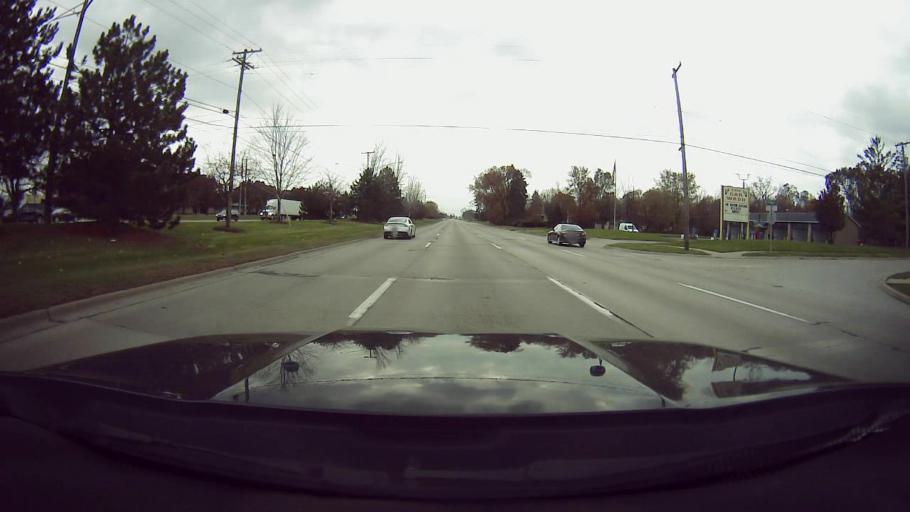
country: US
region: Michigan
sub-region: Macomb County
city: Sterling Heights
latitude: 42.5462
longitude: -83.0481
